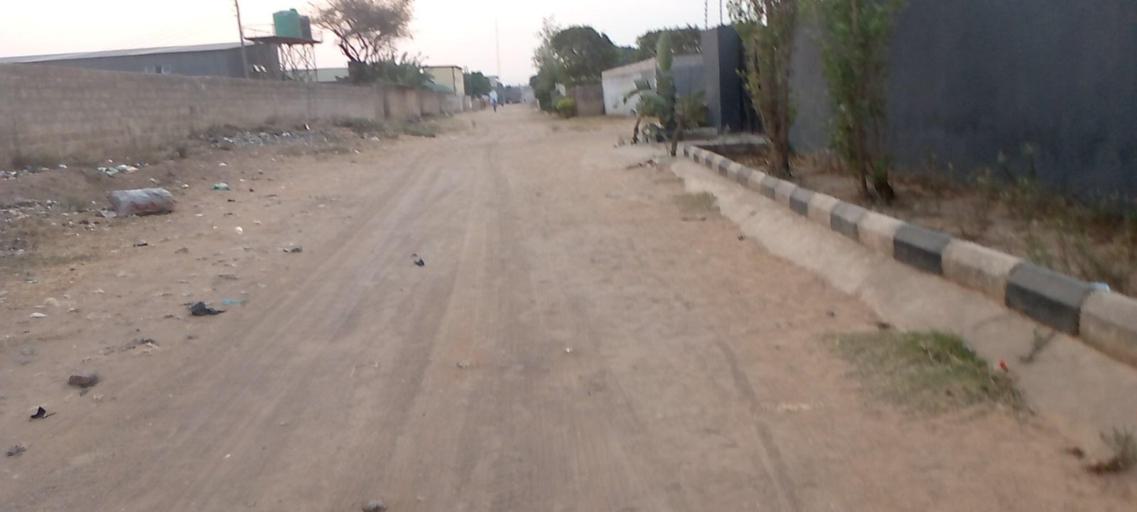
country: ZM
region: Lusaka
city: Lusaka
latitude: -15.4073
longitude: 28.3484
